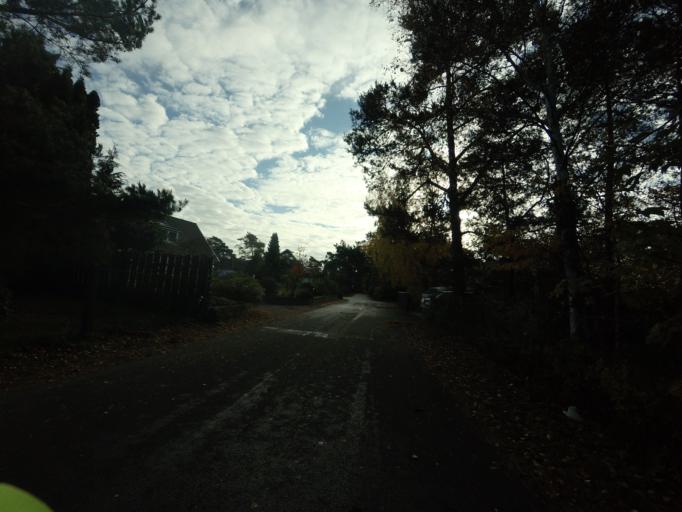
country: SE
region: Skane
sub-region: Vellinge Kommun
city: Hollviken
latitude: 55.4058
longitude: 12.9697
